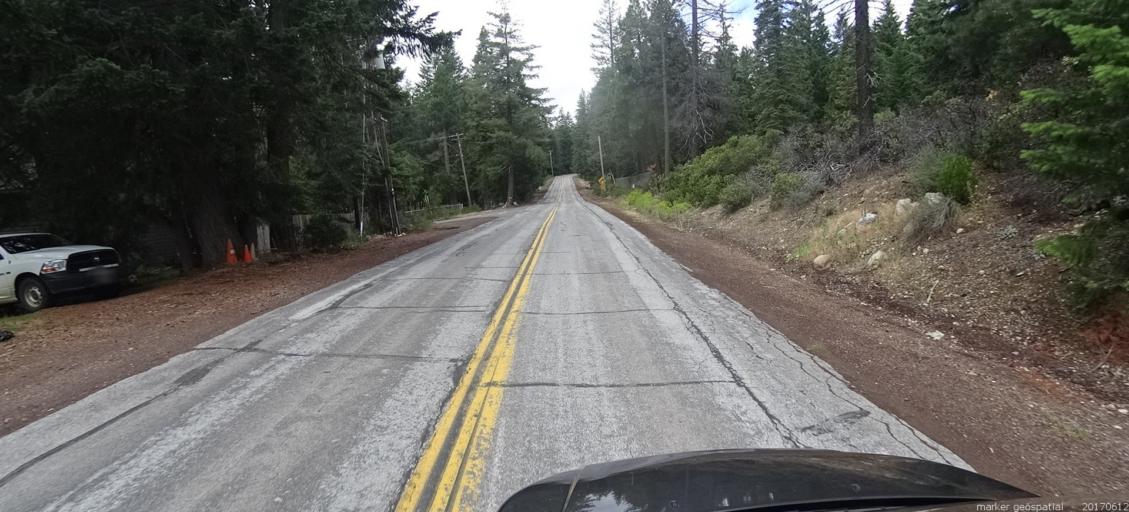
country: US
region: California
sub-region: Siskiyou County
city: Mount Shasta
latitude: 41.3486
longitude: -122.3521
